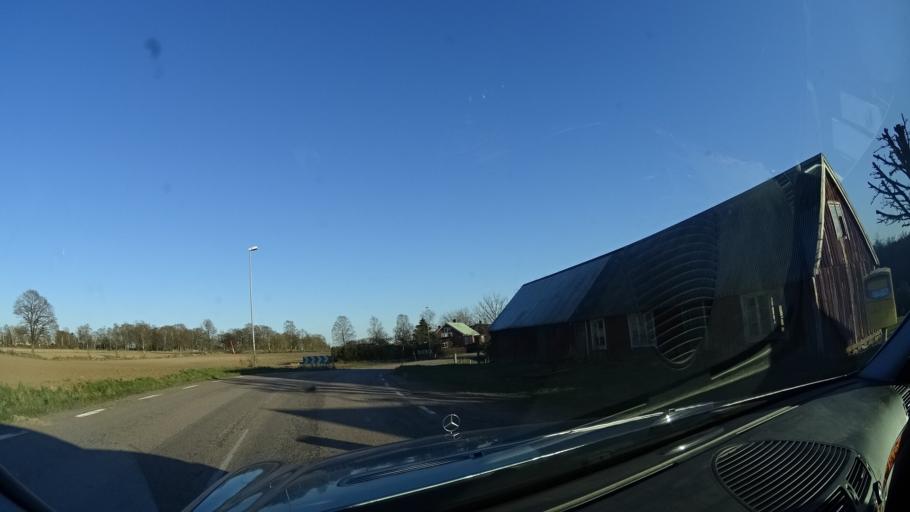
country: SE
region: Skane
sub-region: Bjuvs Kommun
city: Billesholm
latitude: 56.0537
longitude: 12.9976
